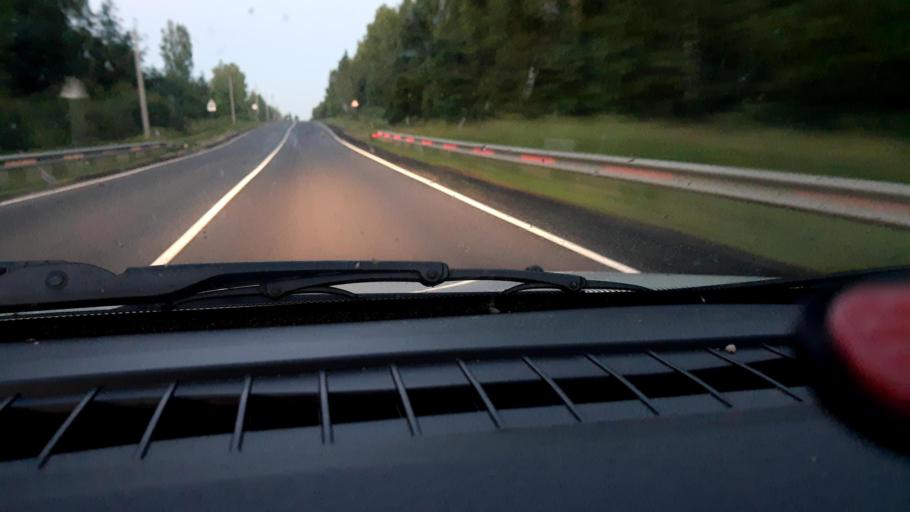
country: RU
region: Nizjnij Novgorod
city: Prudy
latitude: 57.3551
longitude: 46.2217
